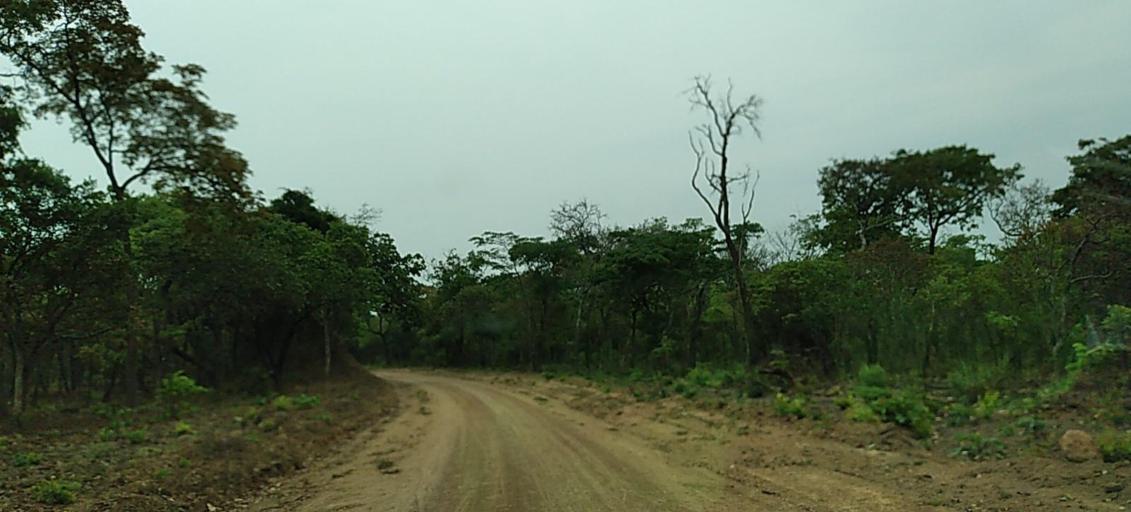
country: ZM
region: North-Western
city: Solwezi
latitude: -12.5247
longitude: 26.5230
